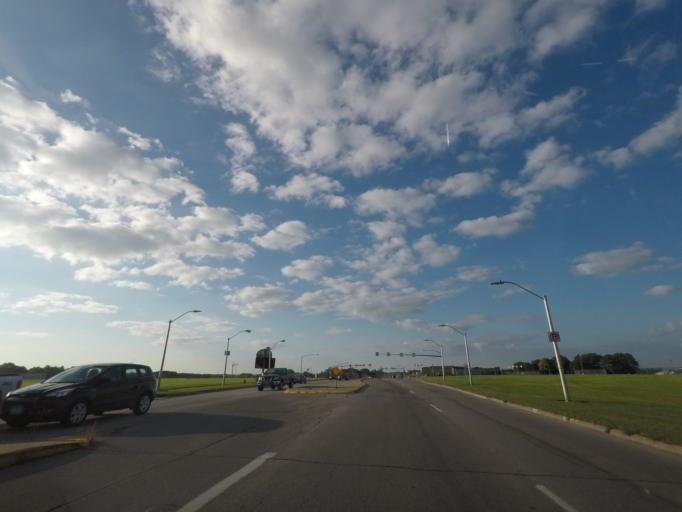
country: US
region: Iowa
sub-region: Warren County
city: Norwalk
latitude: 41.5278
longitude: -93.6449
